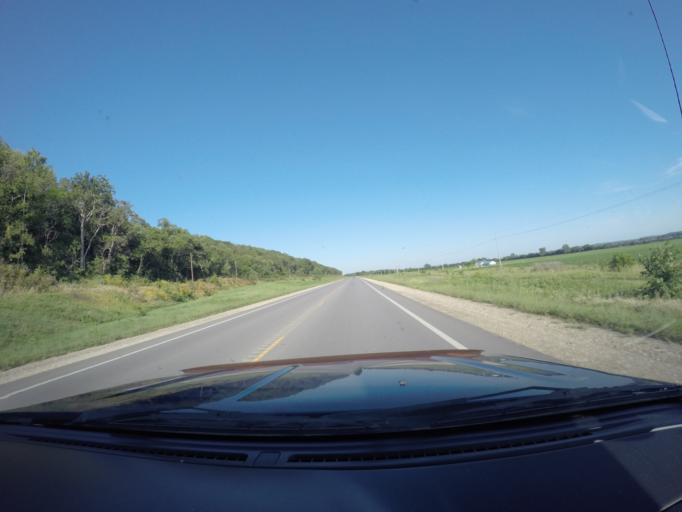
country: US
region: Kansas
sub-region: Jefferson County
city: Oskaloosa
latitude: 39.0728
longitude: -95.3620
